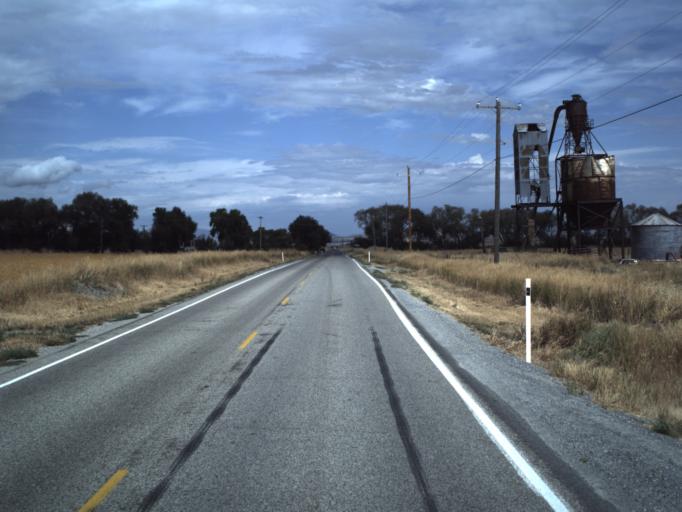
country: US
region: Utah
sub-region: Cache County
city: Mendon
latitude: 41.7406
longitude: -111.9792
